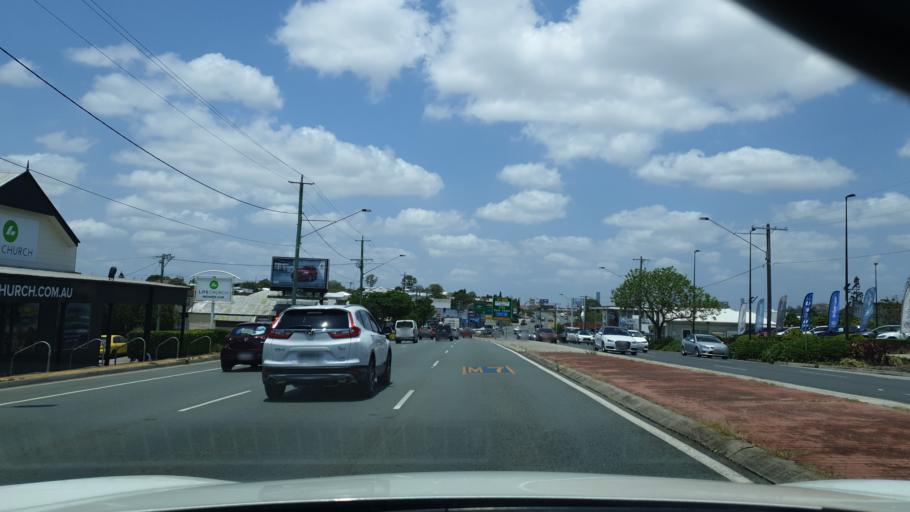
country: AU
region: Queensland
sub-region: Brisbane
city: Gordon Park
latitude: -27.4050
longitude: 153.0321
